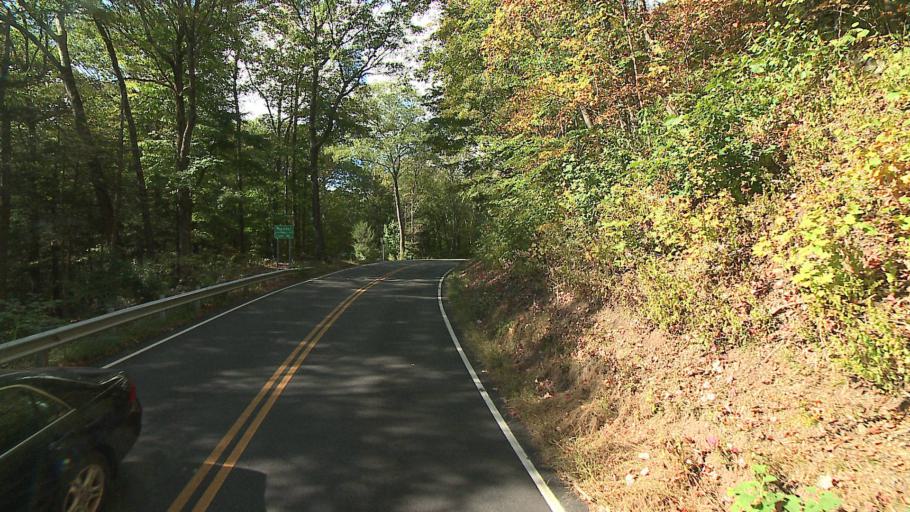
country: US
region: Connecticut
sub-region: New Haven County
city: Prospect
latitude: 41.4676
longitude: -72.9498
